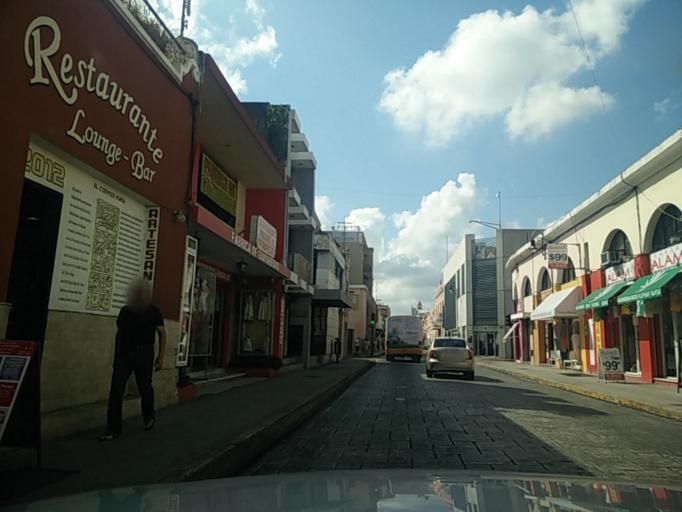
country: MX
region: Yucatan
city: Merida
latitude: 20.9704
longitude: -89.6237
